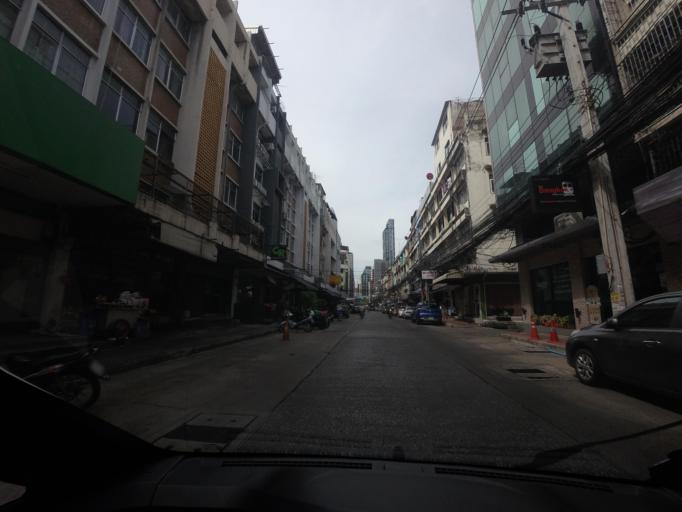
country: TH
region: Bangkok
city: Ratchathewi
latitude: 13.7520
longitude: 100.5457
